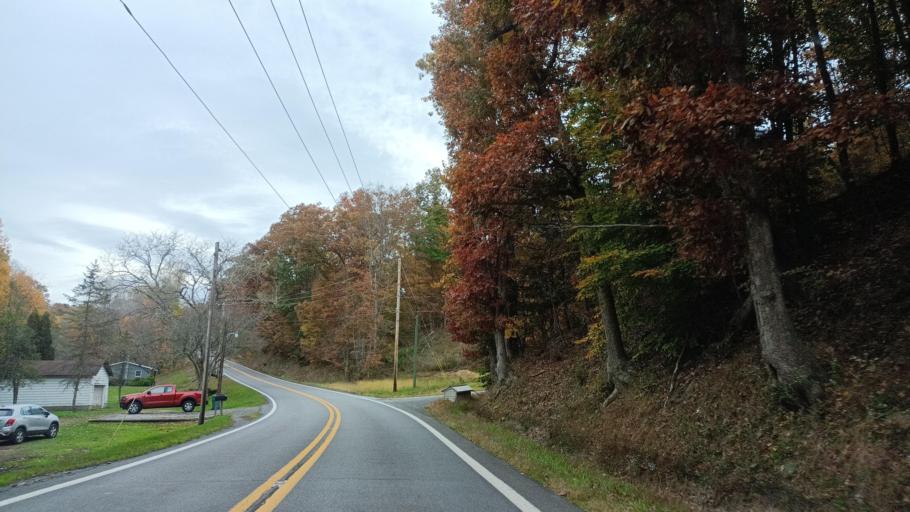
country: US
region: West Virginia
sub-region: Taylor County
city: Grafton
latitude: 39.3295
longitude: -79.9132
